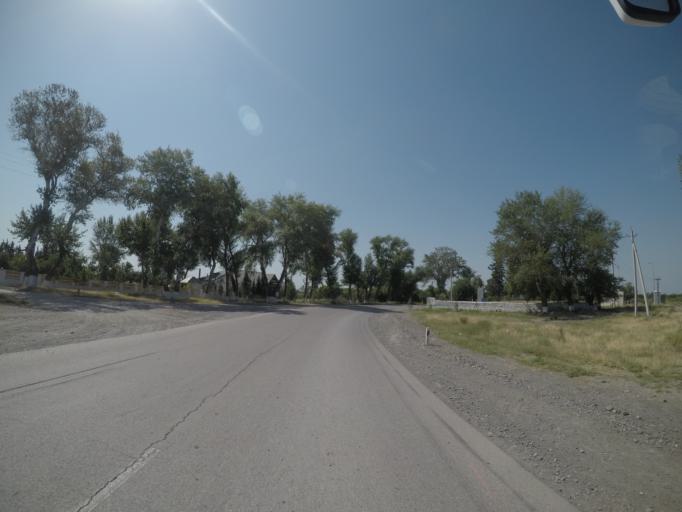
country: AZ
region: Agdas
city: Agdas
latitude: 40.6991
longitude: 47.5423
